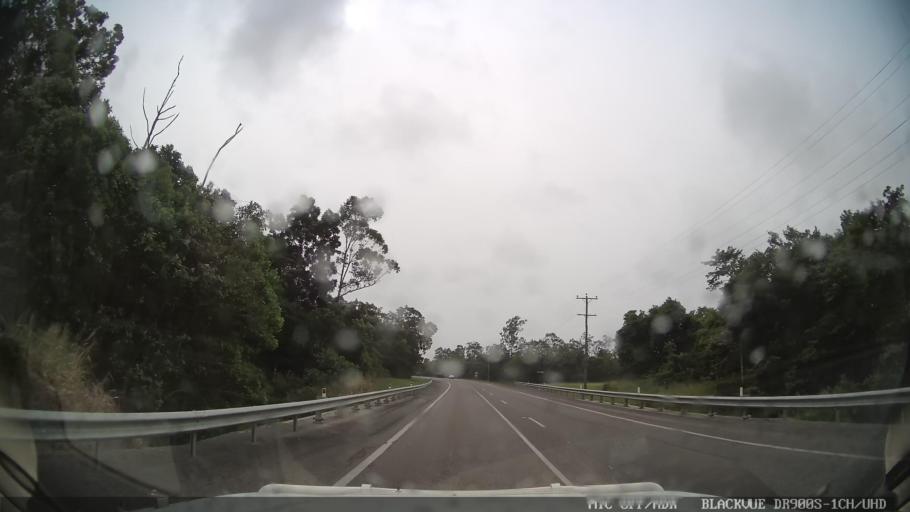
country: AU
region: Queensland
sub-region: Hinchinbrook
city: Ingham
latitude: -18.1208
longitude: 145.9133
